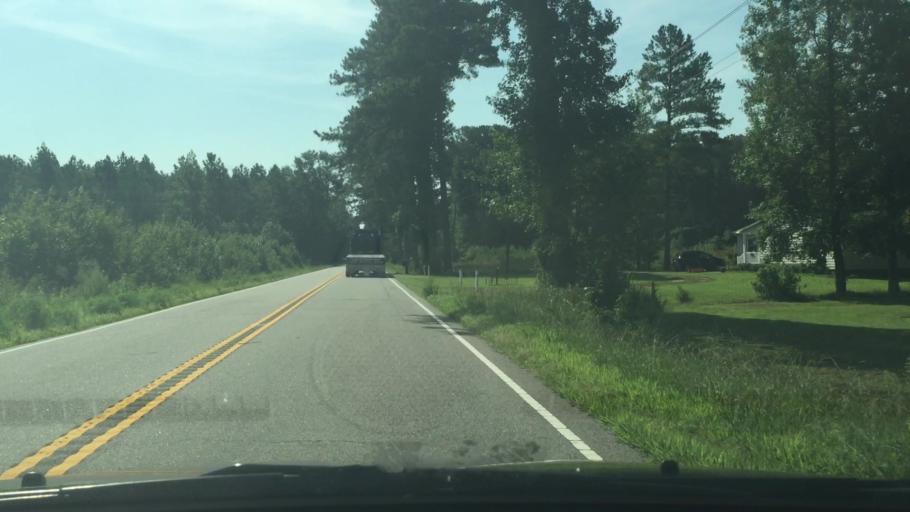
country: US
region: Virginia
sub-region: Sussex County
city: Sussex
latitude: 37.0248
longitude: -77.2910
